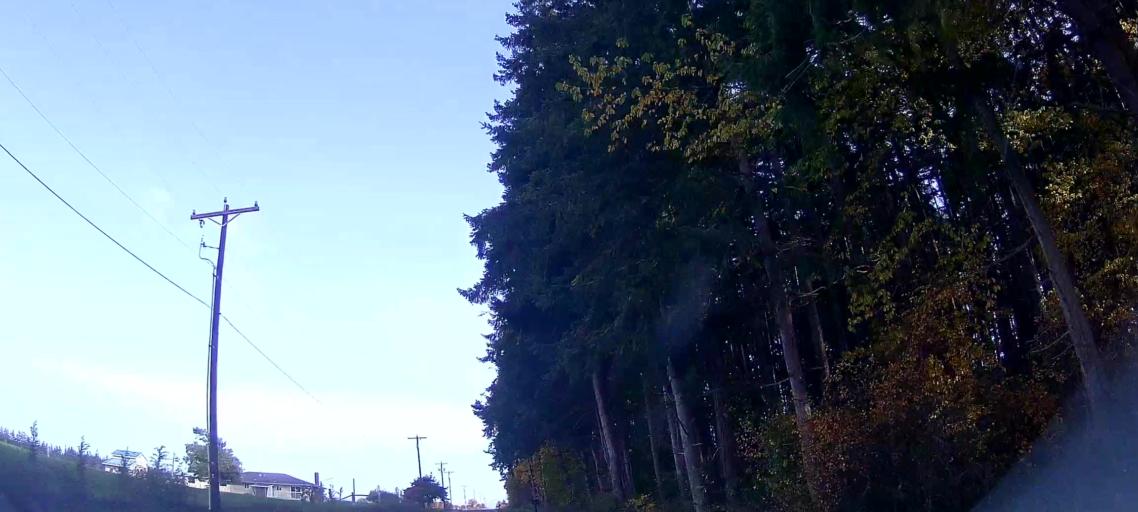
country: US
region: Washington
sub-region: Snohomish County
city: Stanwood
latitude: 48.2545
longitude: -122.4523
